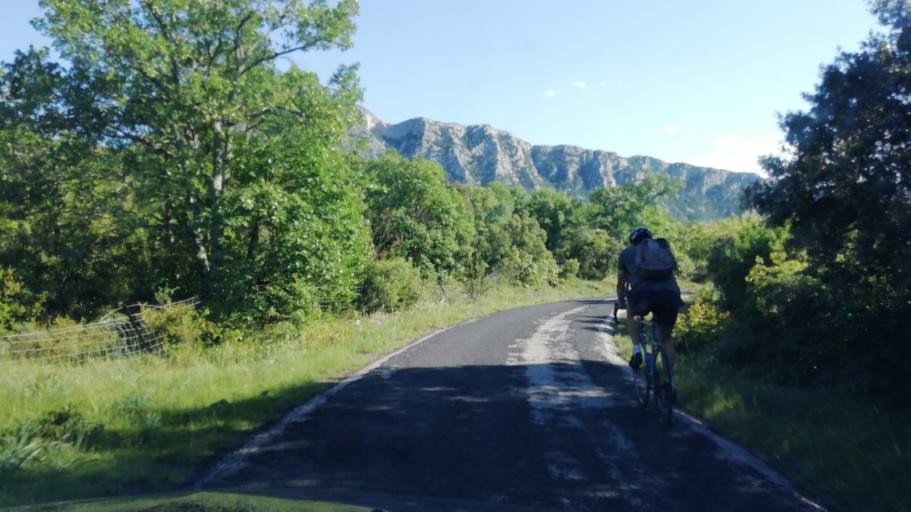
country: FR
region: Languedoc-Roussillon
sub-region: Departement de l'Herault
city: Saint-Mathieu-de-Treviers
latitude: 43.7933
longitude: 3.8099
